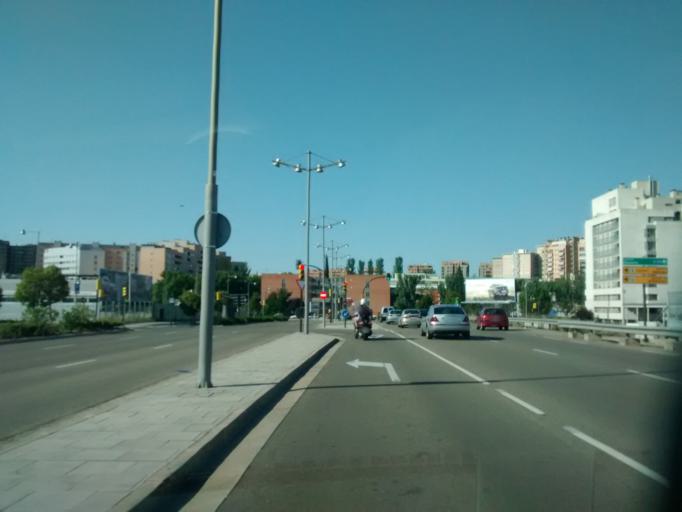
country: ES
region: Aragon
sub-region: Provincia de Zaragoza
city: Delicias
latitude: 41.6598
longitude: -0.9153
